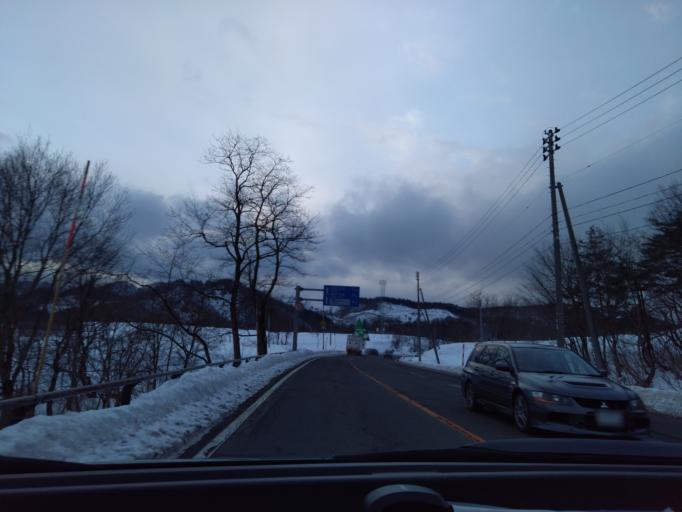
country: JP
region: Akita
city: Yokotemachi
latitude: 39.2733
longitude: 140.7162
